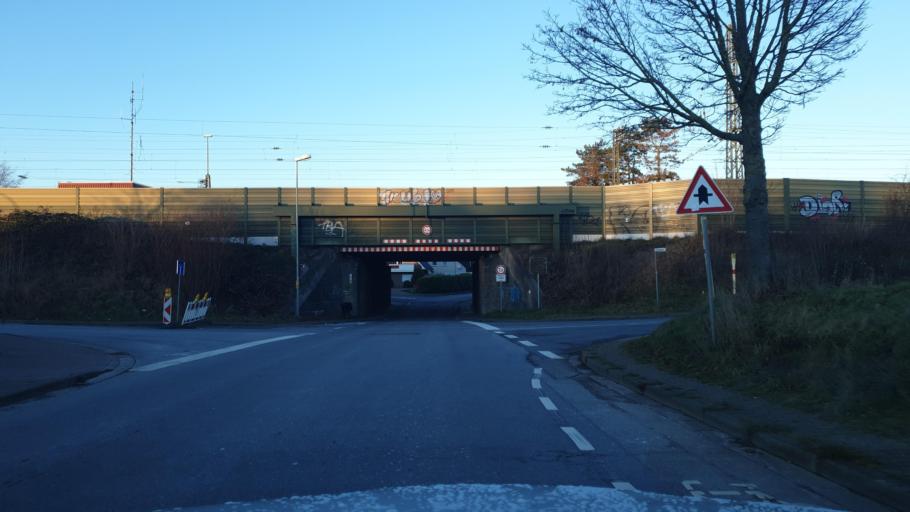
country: DE
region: North Rhine-Westphalia
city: Bad Oeynhausen
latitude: 52.2070
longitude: 8.8226
